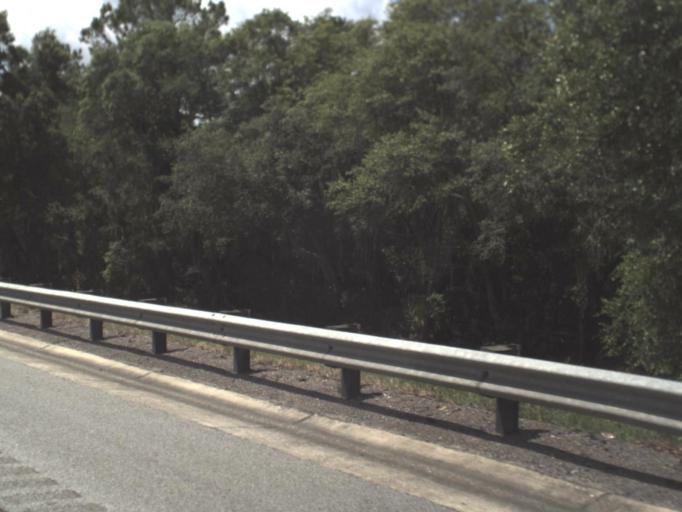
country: US
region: Florida
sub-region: Suwannee County
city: Wellborn
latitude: 30.3451
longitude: -82.8320
